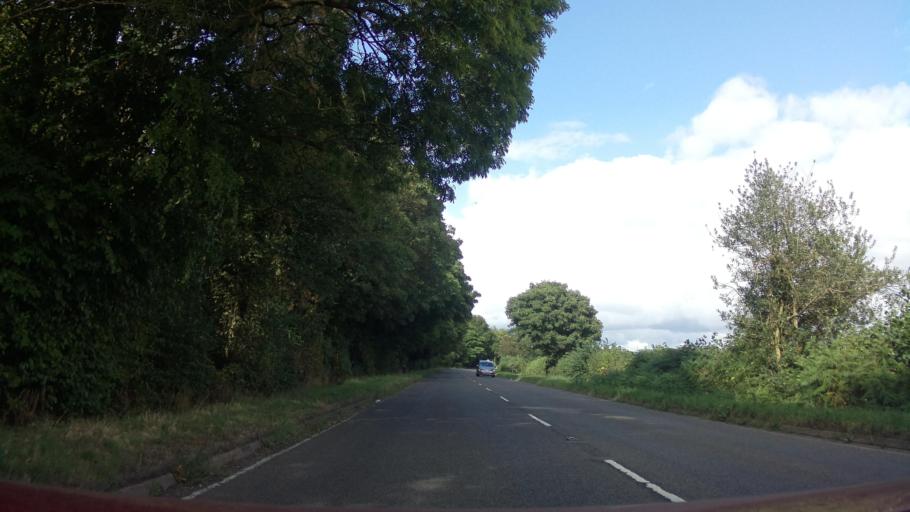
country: GB
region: England
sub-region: Leicestershire
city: Ashby de la Zouch
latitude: 52.7301
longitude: -1.4870
